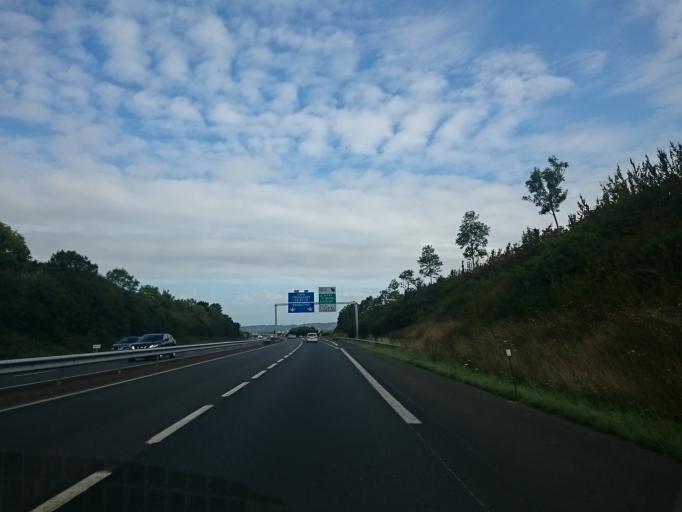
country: FR
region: Lower Normandy
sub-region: Departement de la Manche
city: Saint-Quentin-sur-le-Homme
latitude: 48.6191
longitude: -1.3349
